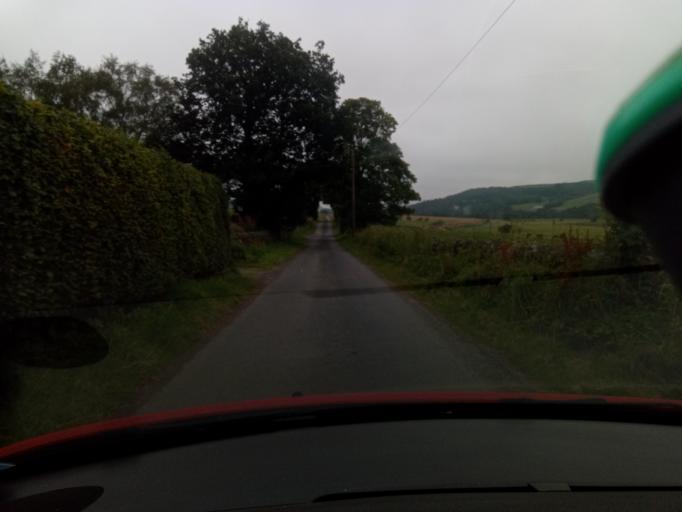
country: GB
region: Scotland
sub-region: The Scottish Borders
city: Galashiels
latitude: 55.6672
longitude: -2.8814
